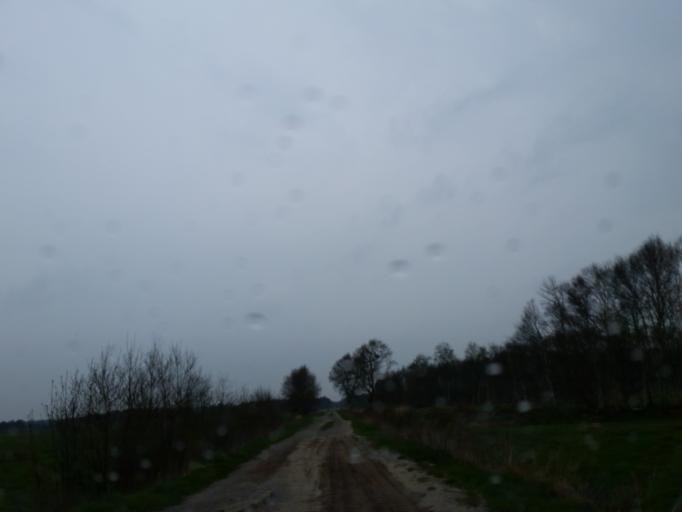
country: DE
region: Lower Saxony
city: Armstorf
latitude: 53.5932
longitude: 9.0061
